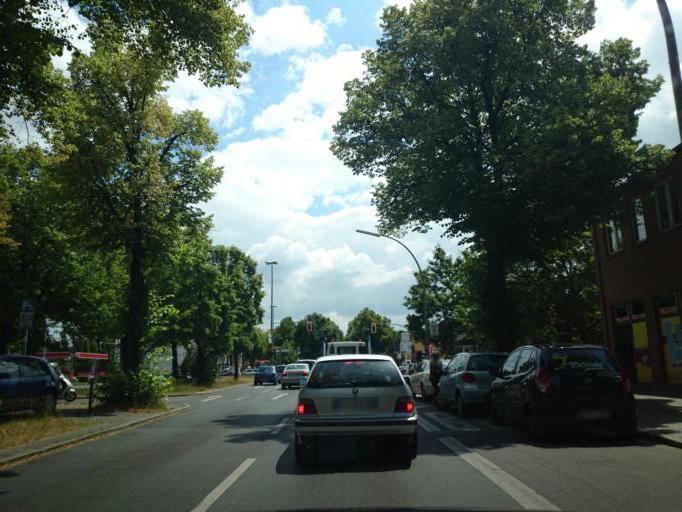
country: DE
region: Berlin
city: Lichtenrade
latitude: 52.4152
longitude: 13.4006
